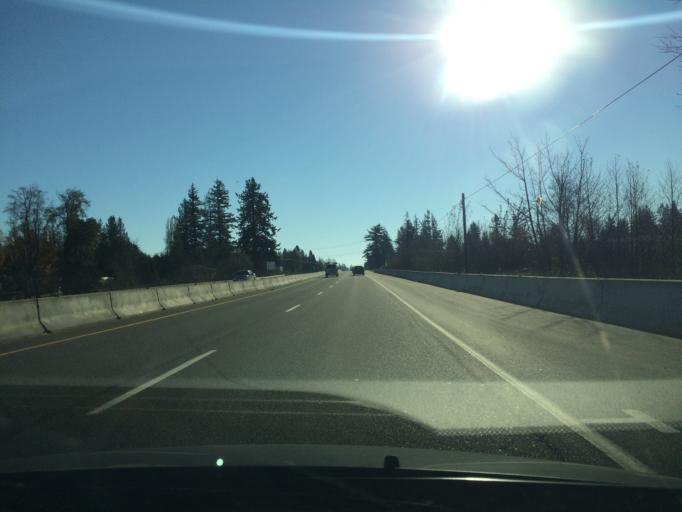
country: US
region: Washington
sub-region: Whatcom County
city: Lynden
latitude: 48.9032
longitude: -122.4856
